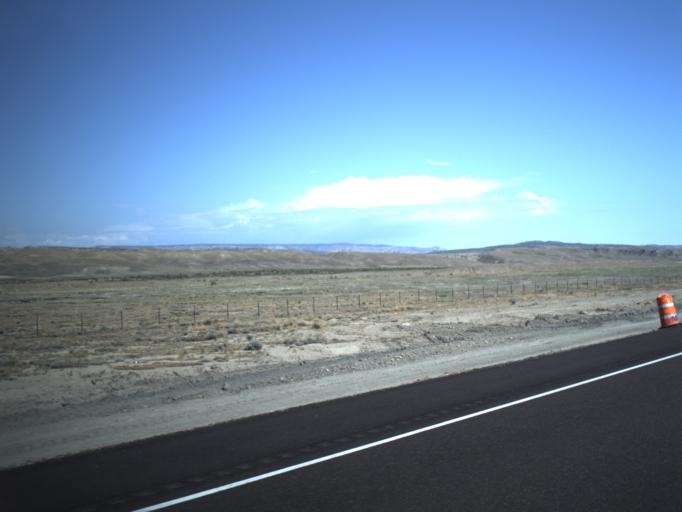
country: US
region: Utah
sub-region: Carbon County
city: East Carbon City
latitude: 39.0518
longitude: -110.3105
